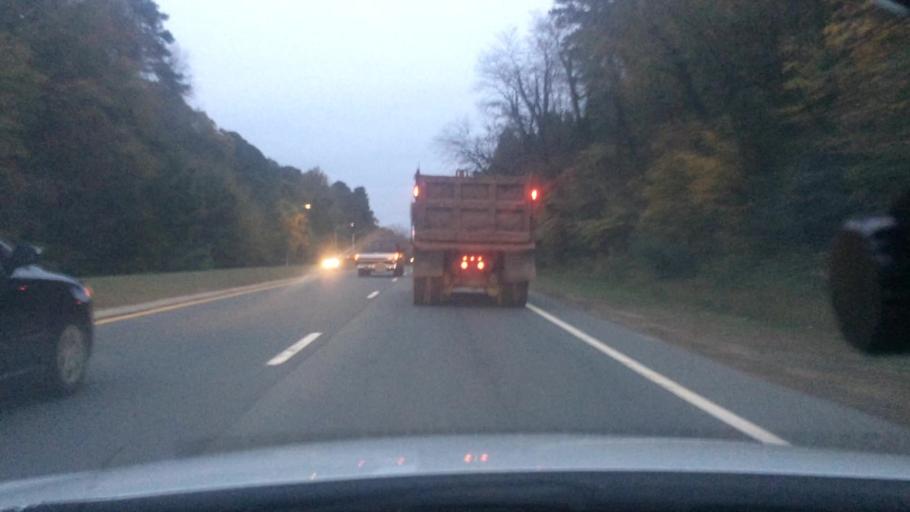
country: US
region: North Carolina
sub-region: Orange County
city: Chapel Hill
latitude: 35.8953
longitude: -79.0483
